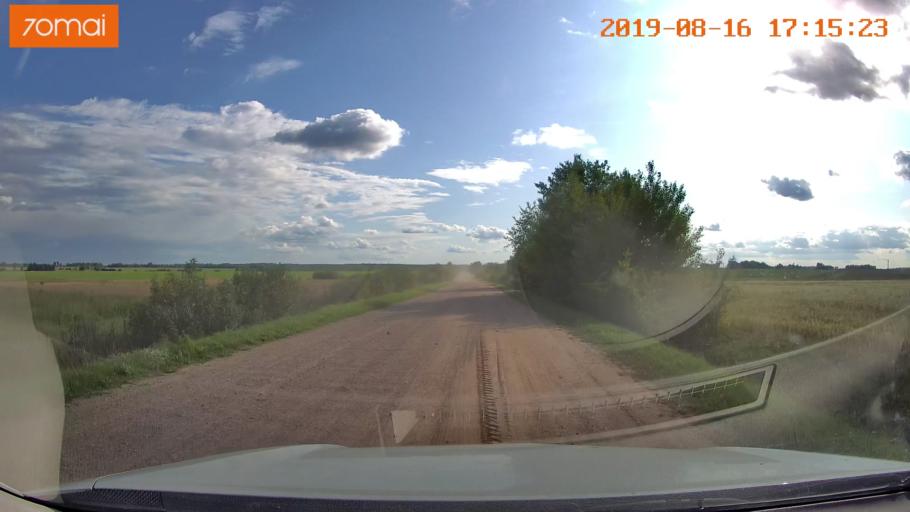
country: BY
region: Mogilev
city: Hlusha
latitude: 53.1792
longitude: 28.8441
